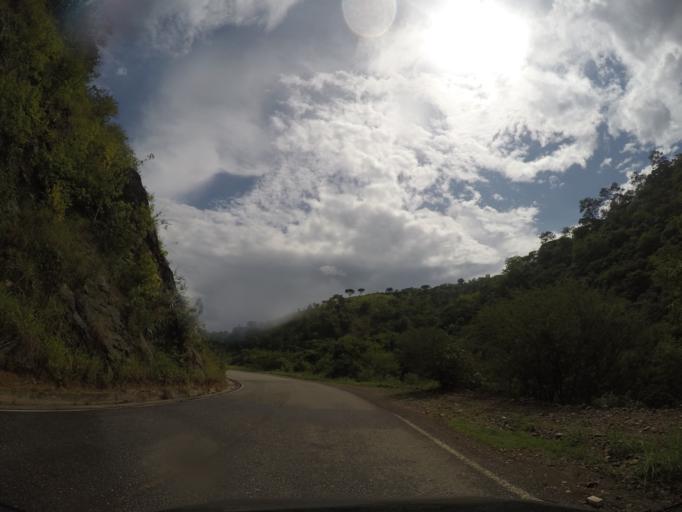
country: MX
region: Oaxaca
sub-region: San Jeronimo Coatlan
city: San Cristobal Honduras
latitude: 16.3818
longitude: -97.0765
